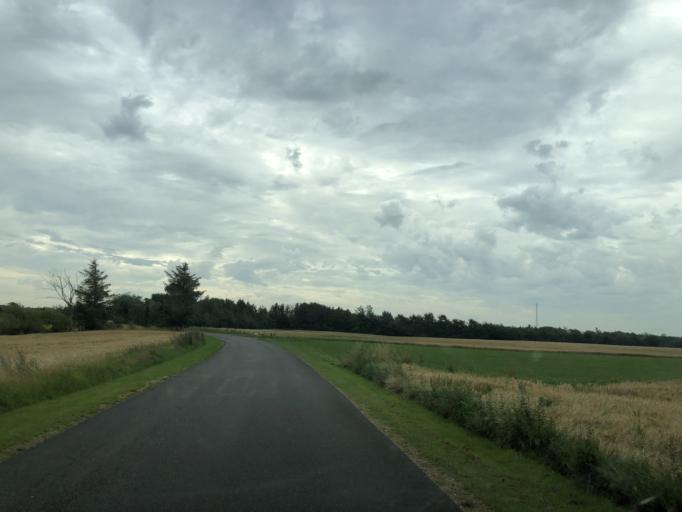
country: DK
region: Central Jutland
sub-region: Holstebro Kommune
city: Holstebro
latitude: 56.3816
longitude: 8.5212
